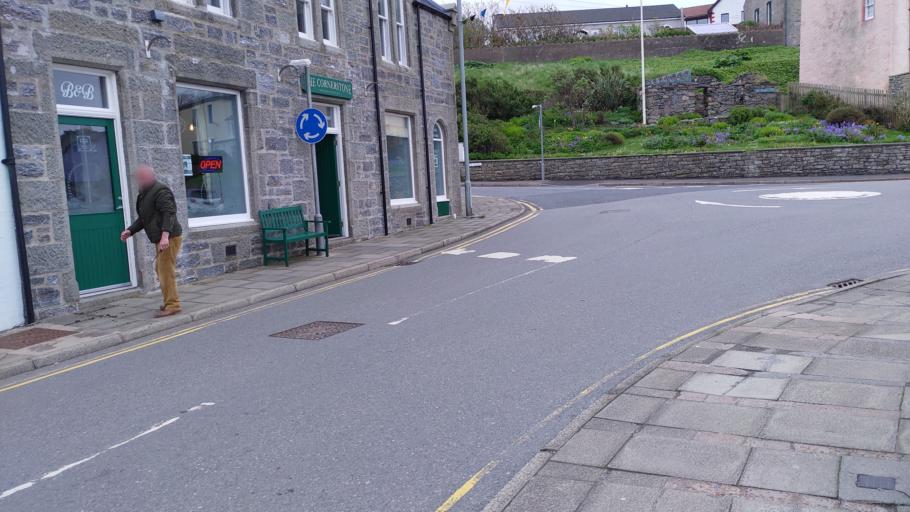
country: GB
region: Scotland
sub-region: Shetland Islands
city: Lerwick
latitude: 60.1370
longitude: -1.2757
